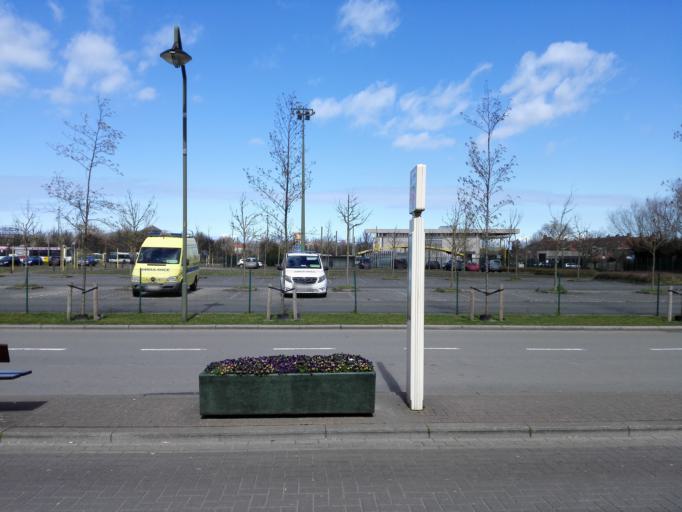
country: BE
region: Flanders
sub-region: Provincie West-Vlaanderen
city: De Panne
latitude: 51.0773
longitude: 2.6011
